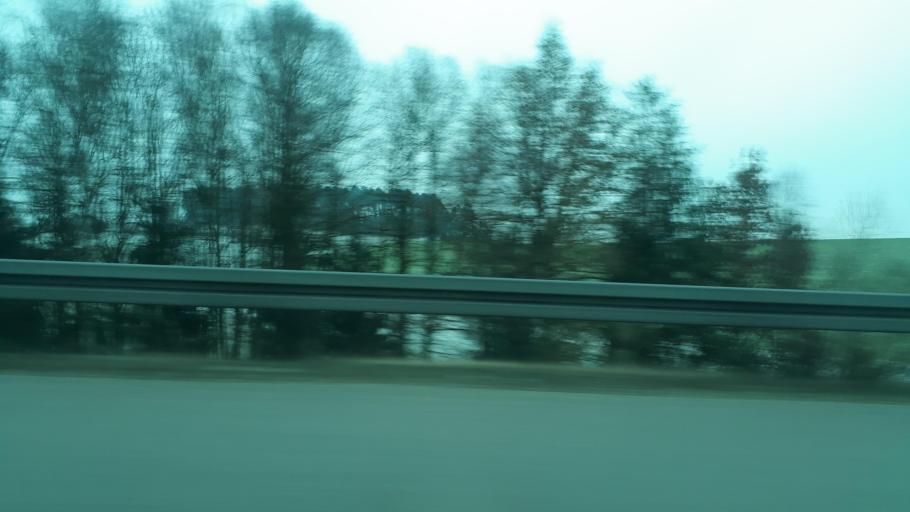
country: DE
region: Bavaria
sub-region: Upper Palatinate
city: Stulln
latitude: 49.4515
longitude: 12.1218
